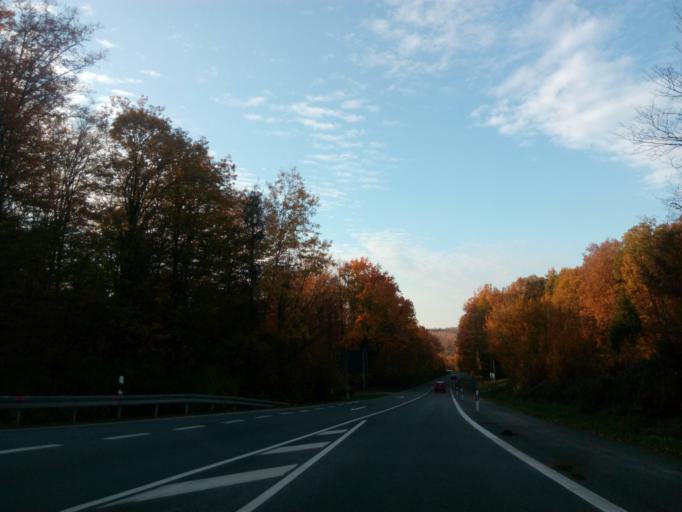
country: DE
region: Saarland
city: Sulzbach
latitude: 49.2838
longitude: 7.0132
